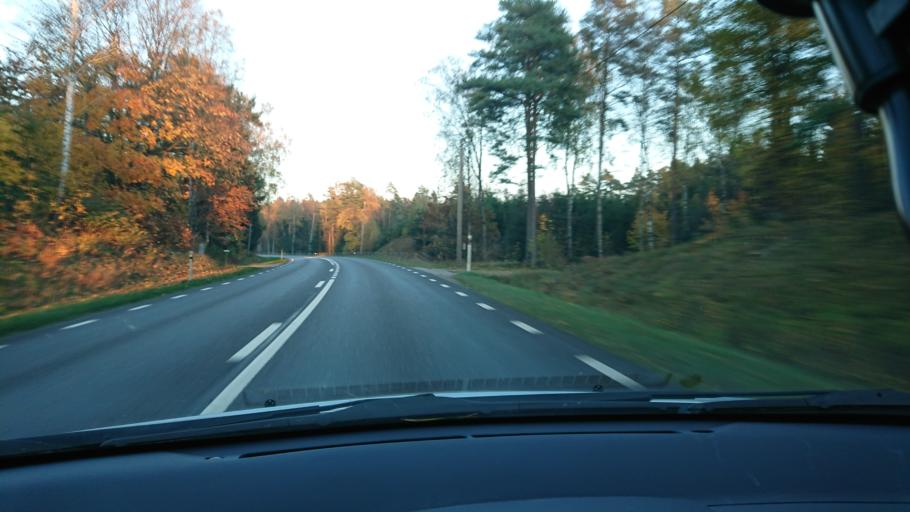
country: SE
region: Halland
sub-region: Halmstads Kommun
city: Oskarstrom
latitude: 56.7131
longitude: 13.1009
